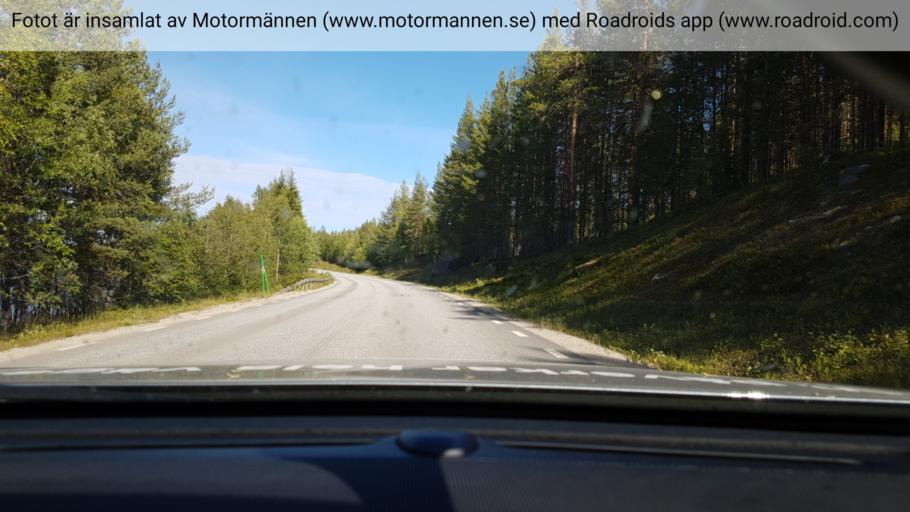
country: SE
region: Vaesterbotten
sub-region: Lycksele Kommun
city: Lycksele
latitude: 64.6280
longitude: 18.5891
